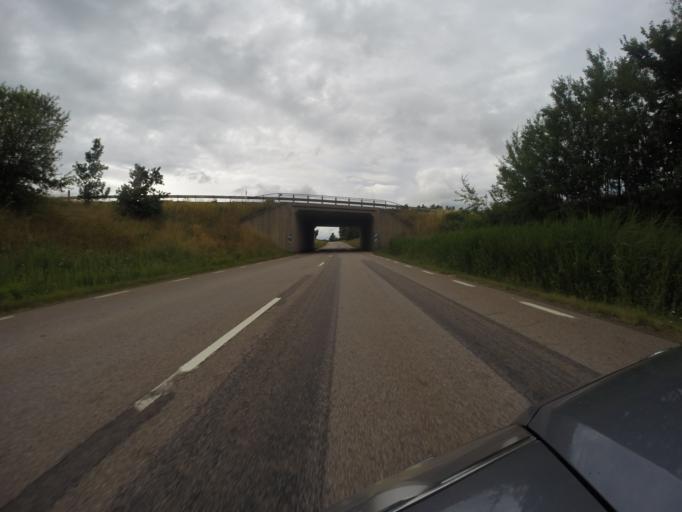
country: SE
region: Skane
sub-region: Helsingborg
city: Hyllinge
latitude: 56.0892
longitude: 12.8045
